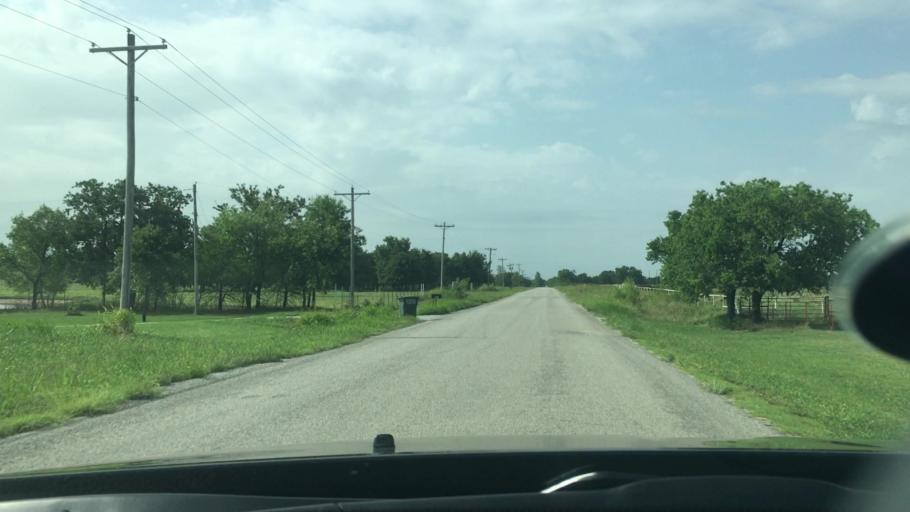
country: US
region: Oklahoma
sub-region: Carter County
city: Lone Grove
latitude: 34.2279
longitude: -97.2737
